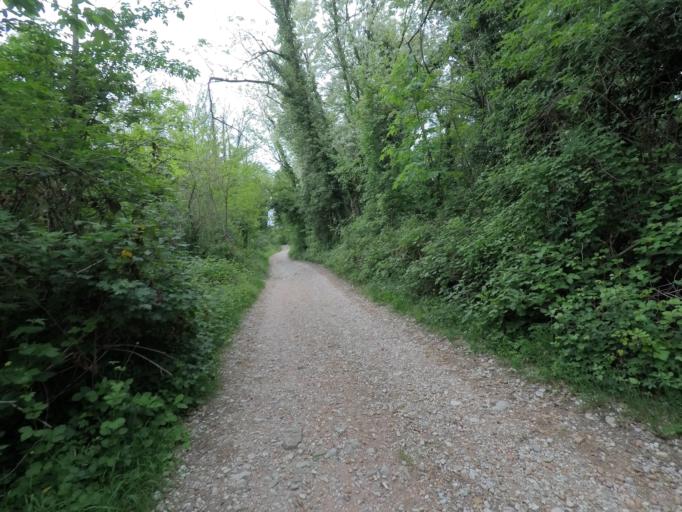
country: IT
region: Friuli Venezia Giulia
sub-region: Provincia di Udine
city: Nimis
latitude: 46.1864
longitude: 13.2452
